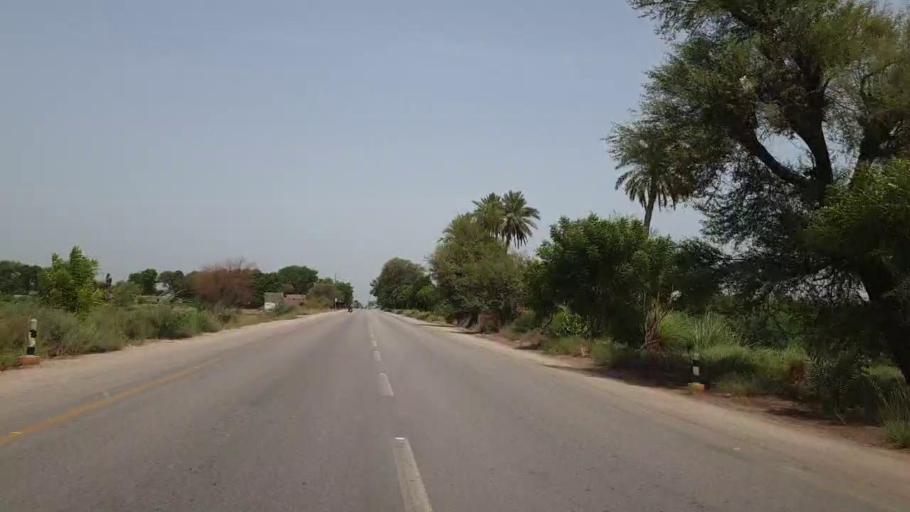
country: PK
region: Sindh
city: Nawabshah
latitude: 26.2202
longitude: 68.5005
